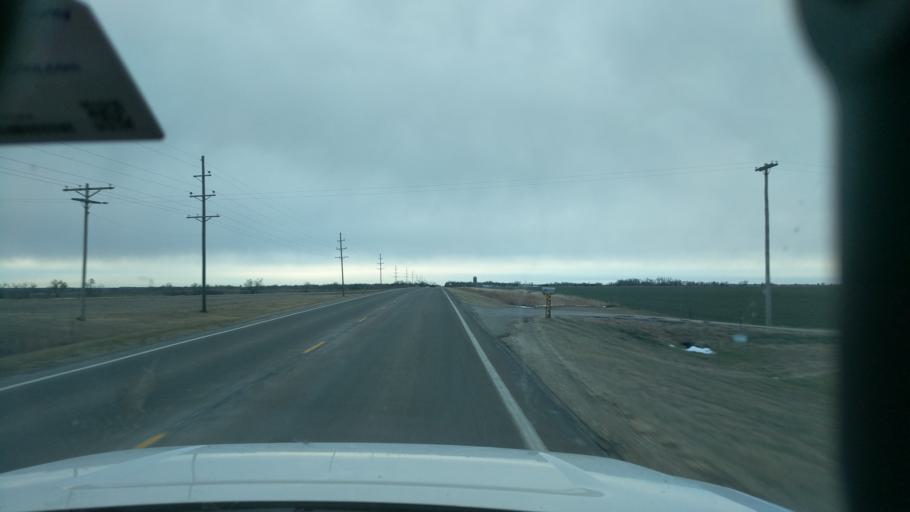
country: US
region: Kansas
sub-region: Marion County
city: Hillsboro
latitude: 38.3121
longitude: -97.3347
